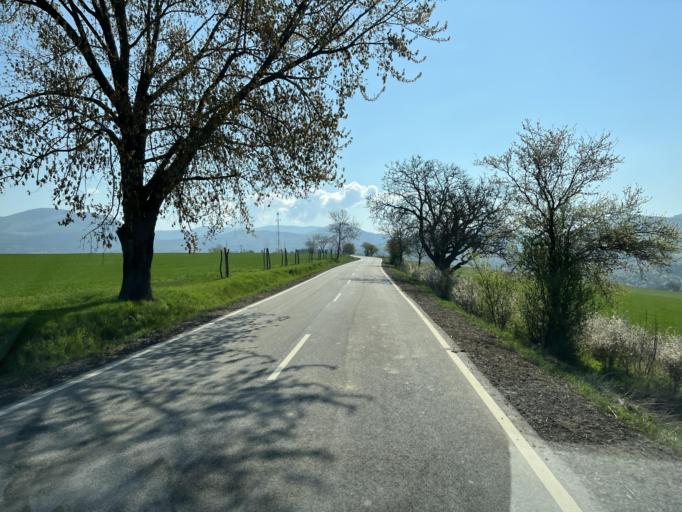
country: HU
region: Pest
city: Szob
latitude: 47.9376
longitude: 18.8057
